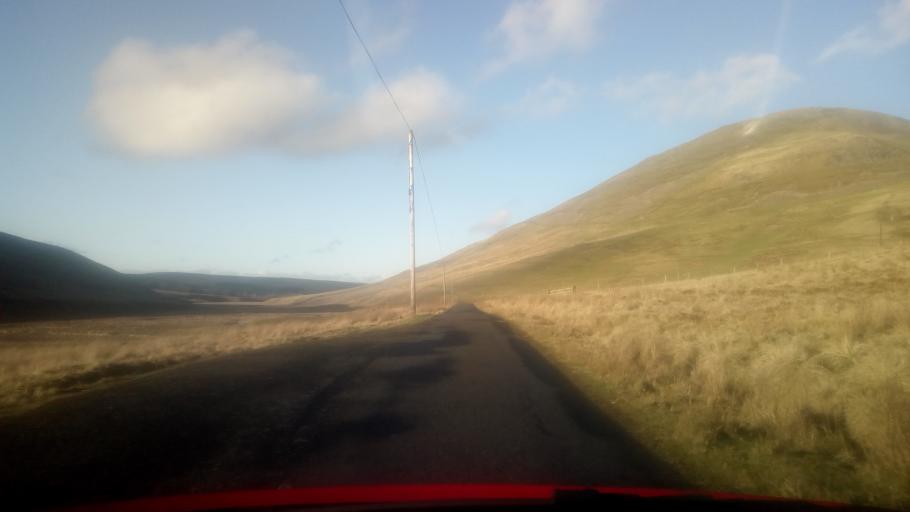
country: GB
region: England
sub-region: Northumberland
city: Rochester
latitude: 55.3980
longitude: -2.3782
